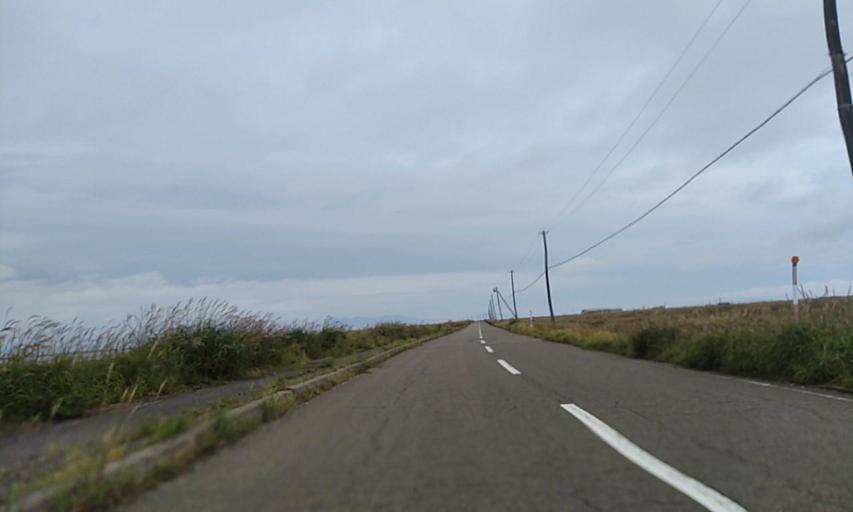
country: JP
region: Hokkaido
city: Shibetsu
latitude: 43.5725
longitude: 145.3441
